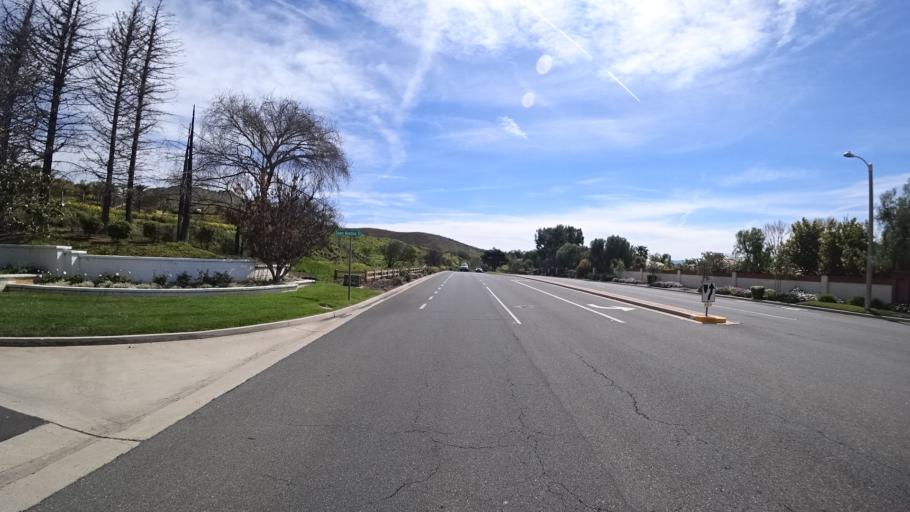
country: US
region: California
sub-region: Ventura County
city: Thousand Oaks
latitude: 34.1961
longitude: -118.8061
